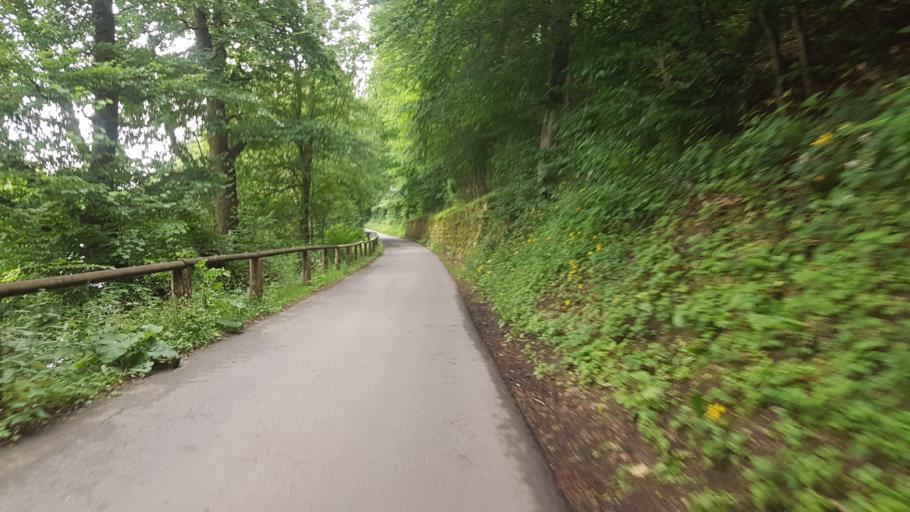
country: DE
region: Baden-Wuerttemberg
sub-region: Tuebingen Region
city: Sigmaringen
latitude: 48.0717
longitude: 9.2418
